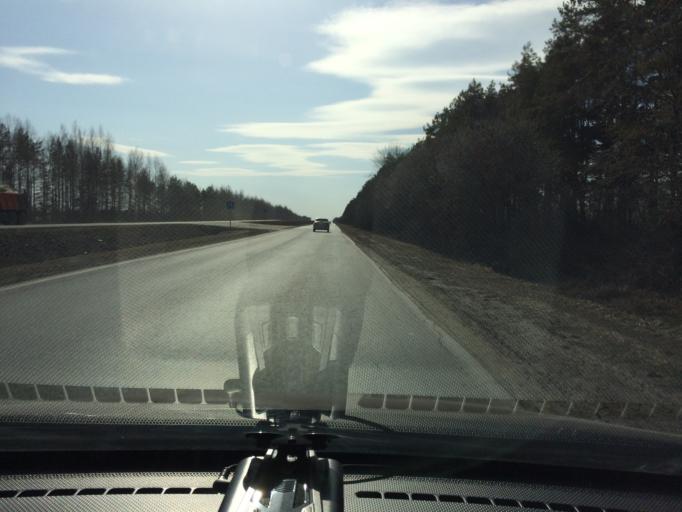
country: RU
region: Mariy-El
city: Yoshkar-Ola
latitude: 56.7267
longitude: 48.1298
